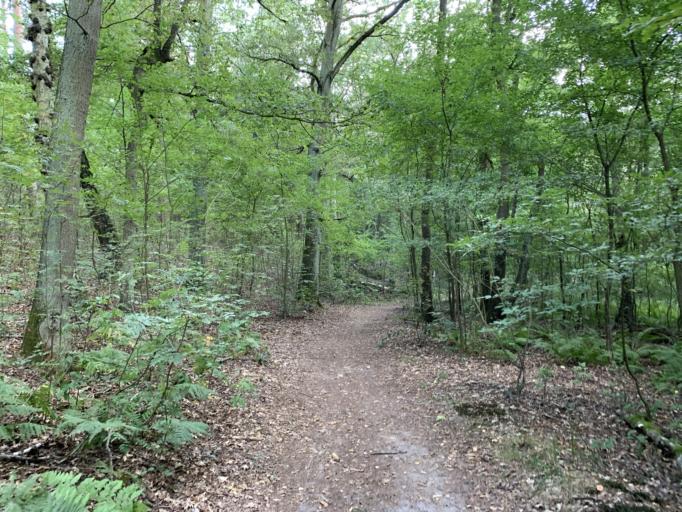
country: DE
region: Brandenburg
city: Michendorf
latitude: 52.3120
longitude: 12.9803
